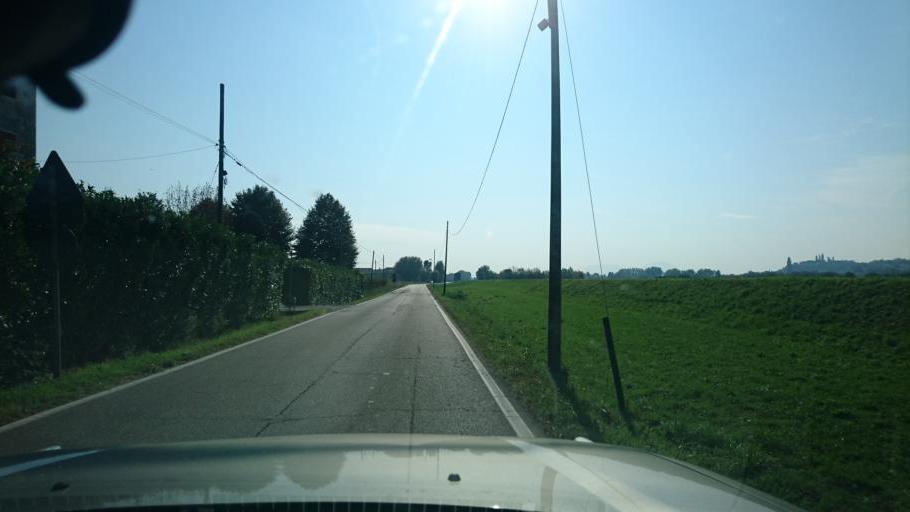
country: IT
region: Veneto
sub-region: Provincia di Vicenza
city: Longare
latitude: 45.4902
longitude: 11.6060
